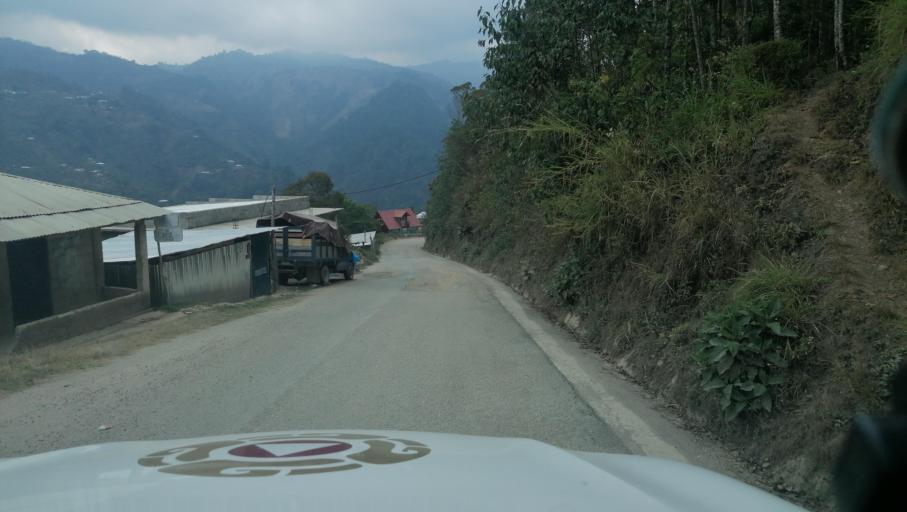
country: GT
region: San Marcos
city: Tacana
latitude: 15.2064
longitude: -92.1907
